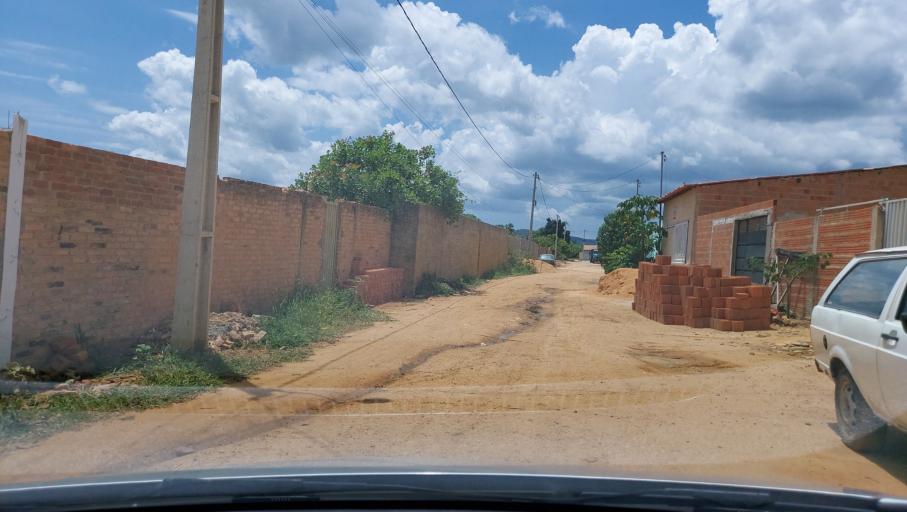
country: BR
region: Bahia
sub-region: Oliveira Dos Brejinhos
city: Beira Rio
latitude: -12.0046
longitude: -42.6297
